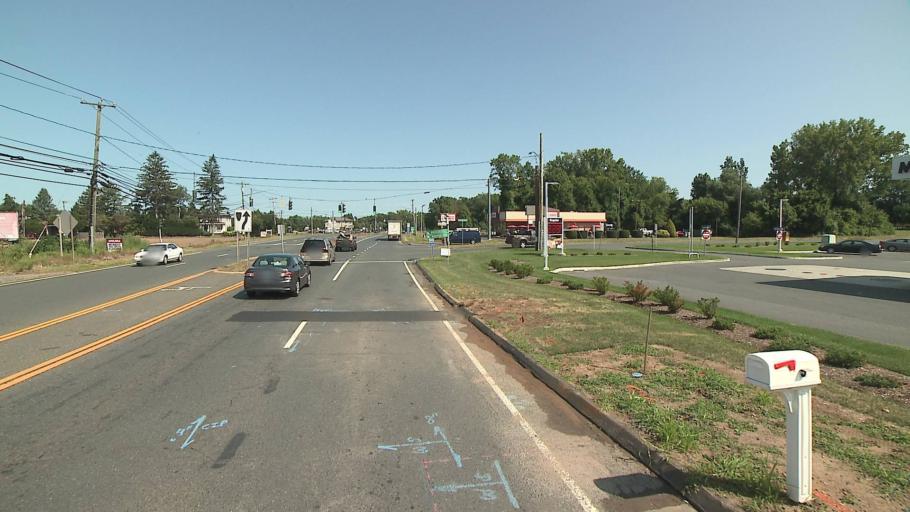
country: US
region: Connecticut
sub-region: Hartford County
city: Windsor Locks
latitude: 41.9120
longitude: -72.6132
